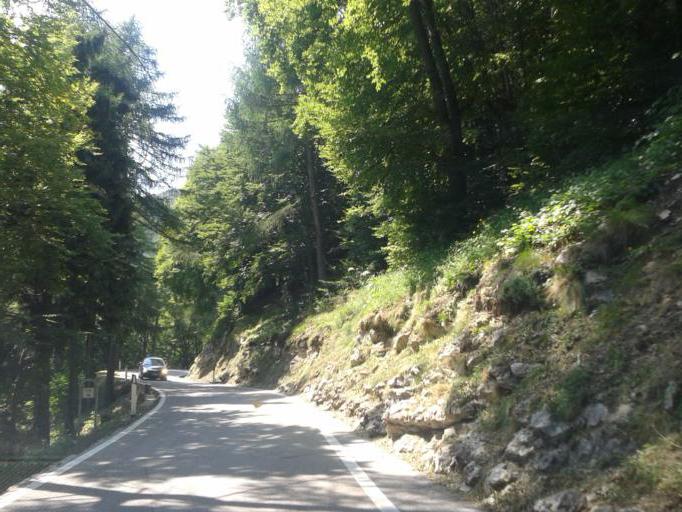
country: IT
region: Trentino-Alto Adige
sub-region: Provincia di Trento
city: Avio
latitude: 45.7849
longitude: 10.9010
